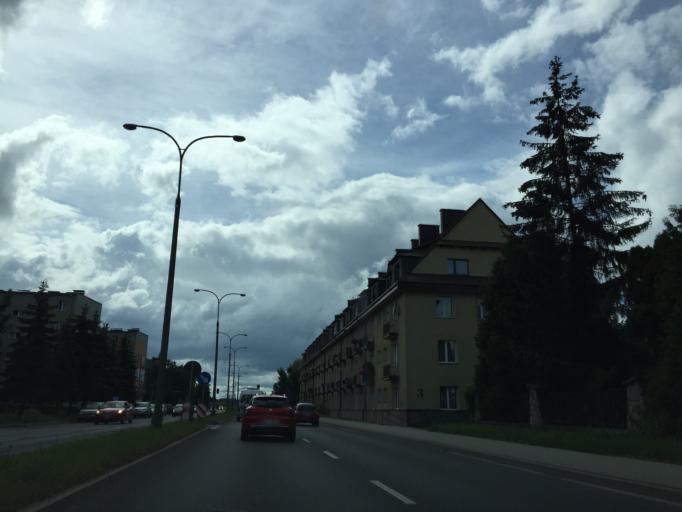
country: PL
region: Lesser Poland Voivodeship
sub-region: Powiat nowotarski
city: Nowy Targ
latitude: 49.4775
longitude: 20.0296
